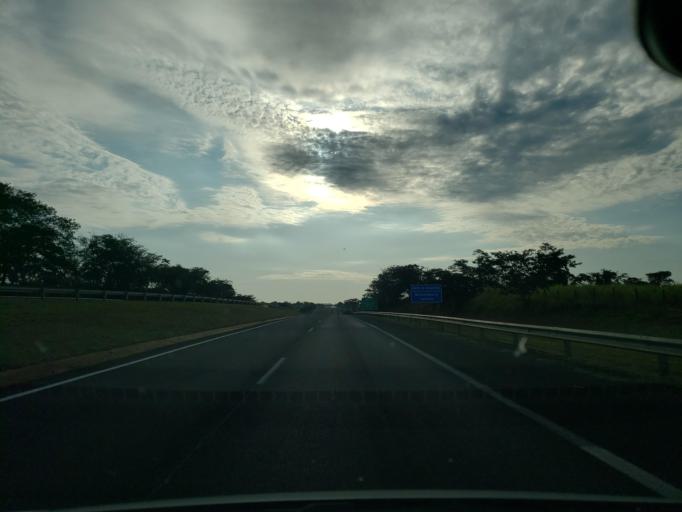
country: BR
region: Sao Paulo
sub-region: Mirandopolis
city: Mirandopolis
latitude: -21.0943
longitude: -51.0499
